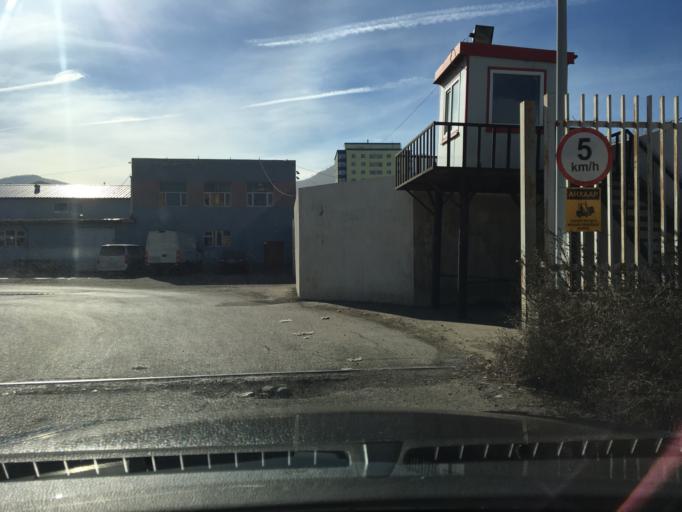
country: MN
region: Ulaanbaatar
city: Ulaanbaatar
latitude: 47.8954
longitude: 106.8974
